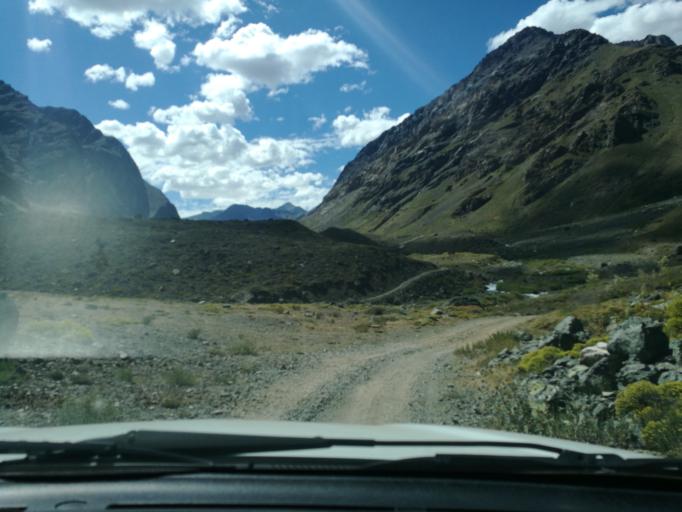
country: CL
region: O'Higgins
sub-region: Provincia de Cachapoal
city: Machali
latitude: -34.4104
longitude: -70.2342
